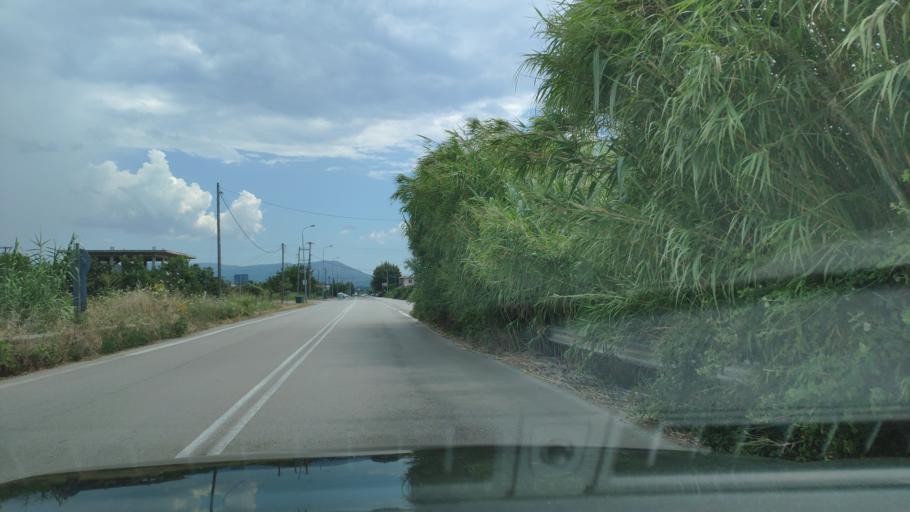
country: GR
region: West Greece
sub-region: Nomos Aitolias kai Akarnanias
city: Krikellos
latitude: 38.9514
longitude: 21.1760
